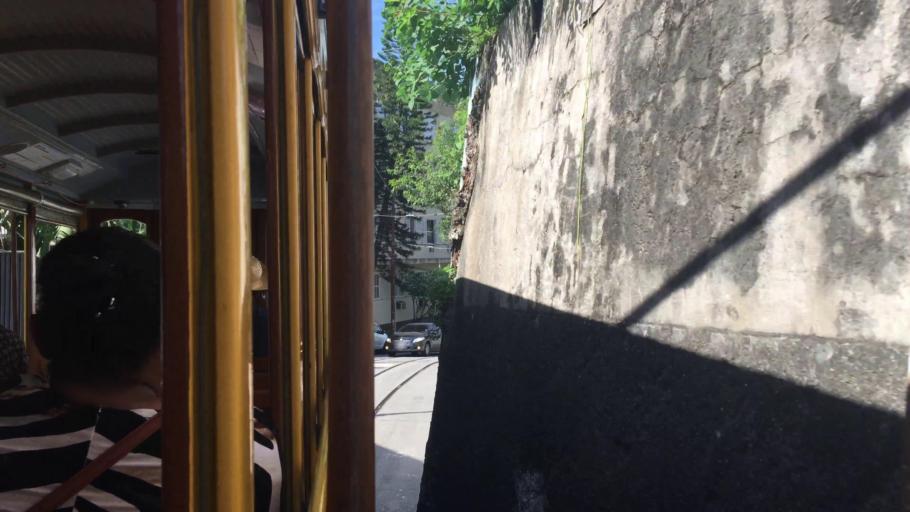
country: BR
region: Rio de Janeiro
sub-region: Rio De Janeiro
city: Rio de Janeiro
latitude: -22.9221
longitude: -43.1877
